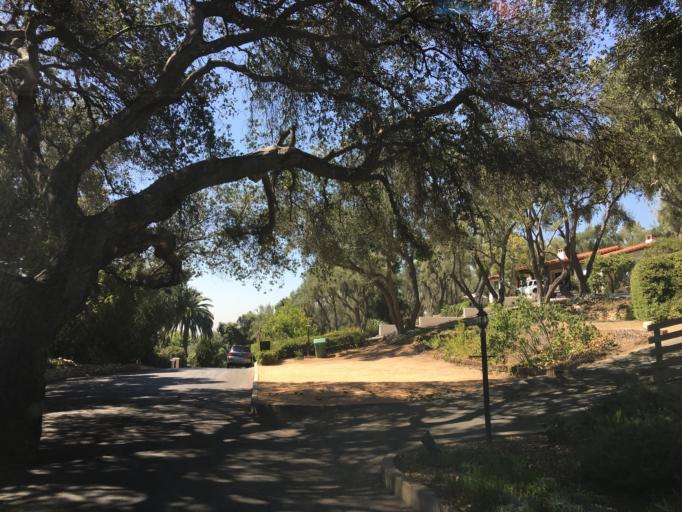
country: US
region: California
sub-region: Los Angeles County
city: La Verne
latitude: 34.1248
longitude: -117.7422
